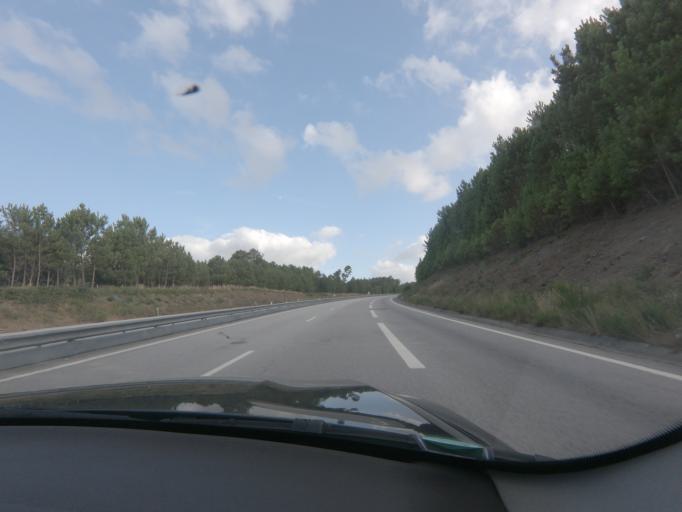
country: PT
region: Viseu
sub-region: Viseu
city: Campo
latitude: 40.7340
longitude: -7.9225
